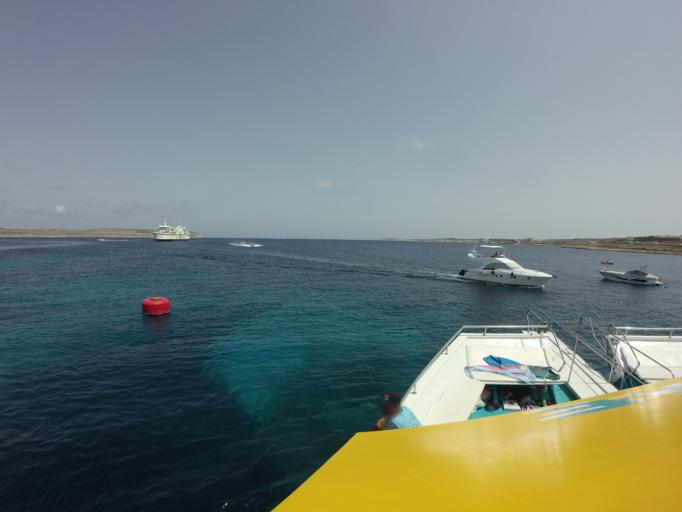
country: MT
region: Il-Mellieha
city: Mellieha
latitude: 35.9888
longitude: 14.3303
